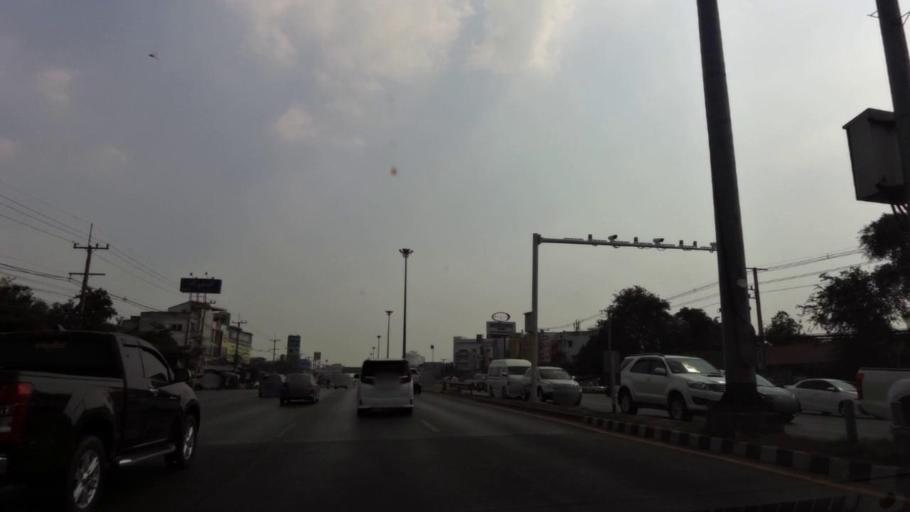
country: TH
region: Phra Nakhon Si Ayutthaya
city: Phra Nakhon Si Ayutthaya
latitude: 14.3530
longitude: 100.6006
